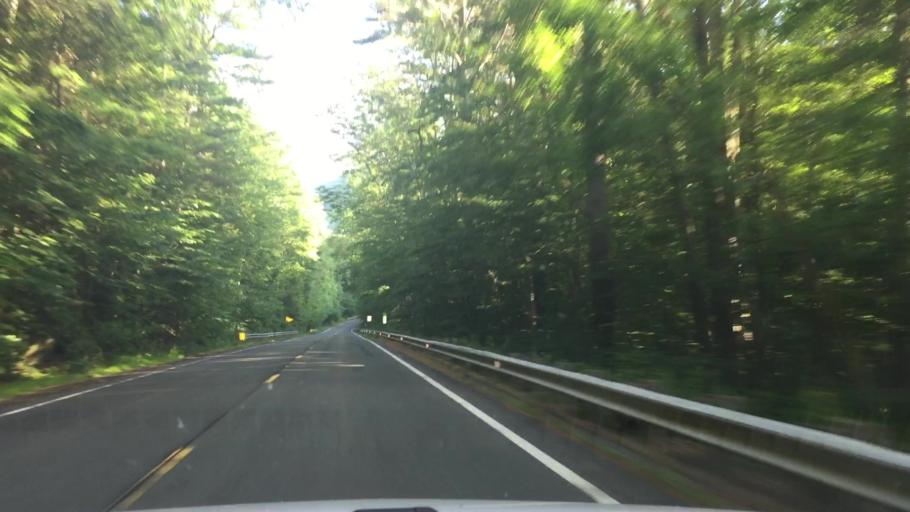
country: US
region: Massachusetts
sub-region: Hampshire County
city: Chesterfield
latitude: 42.3207
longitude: -72.8697
